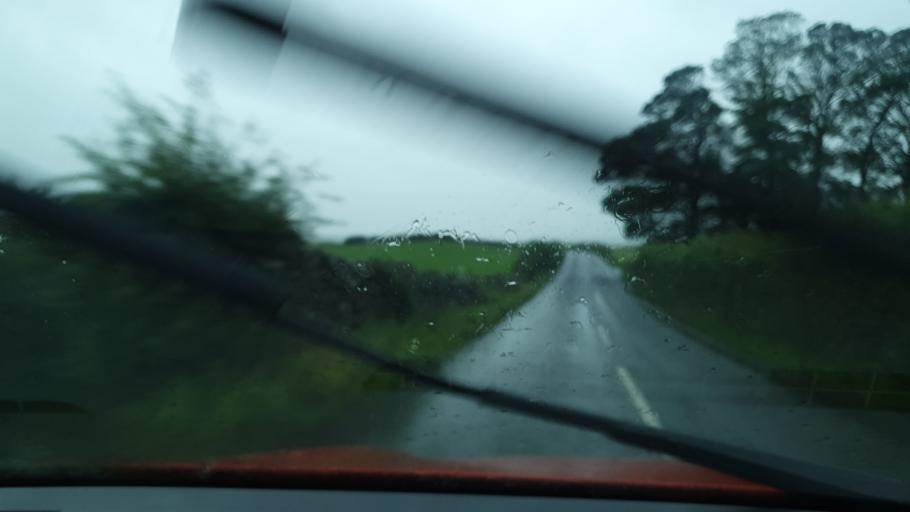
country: GB
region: England
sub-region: Cumbria
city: Millom
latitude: 54.2765
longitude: -3.2205
